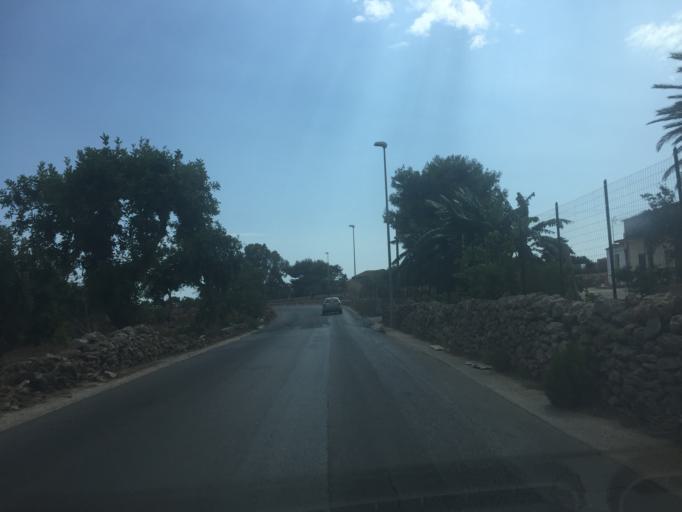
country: IT
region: Sicily
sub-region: Ragusa
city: Santa Croce Camerina
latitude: 36.8196
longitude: 14.5177
